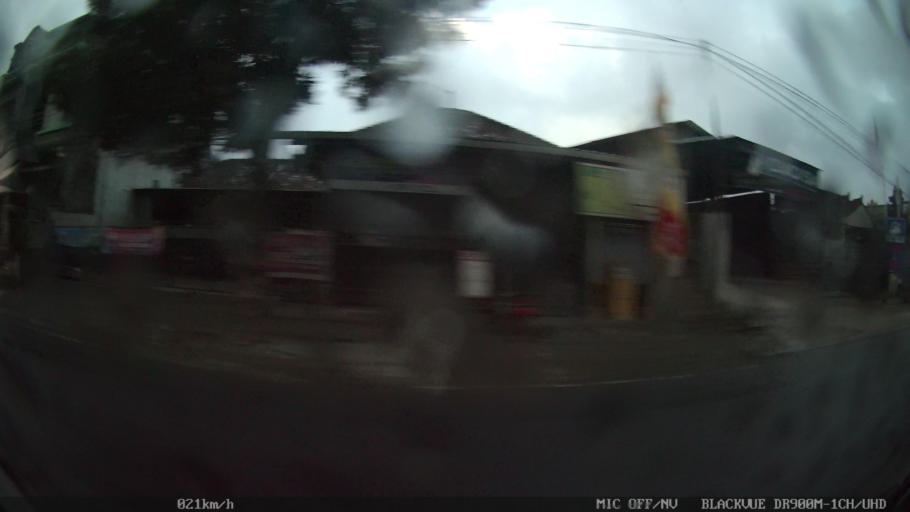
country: ID
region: Bali
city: Banjar Batur
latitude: -8.5895
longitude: 115.2154
